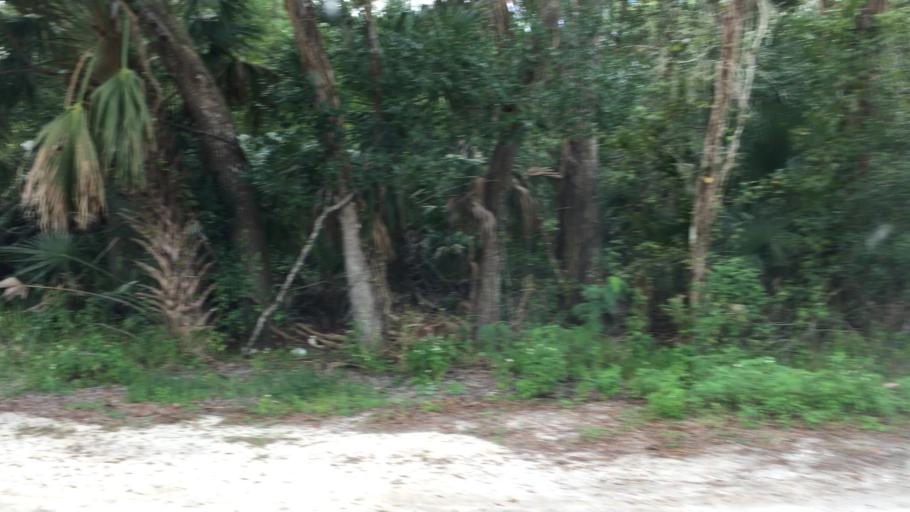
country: US
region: Florida
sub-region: Volusia County
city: Glencoe
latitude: 29.0170
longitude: -80.9715
